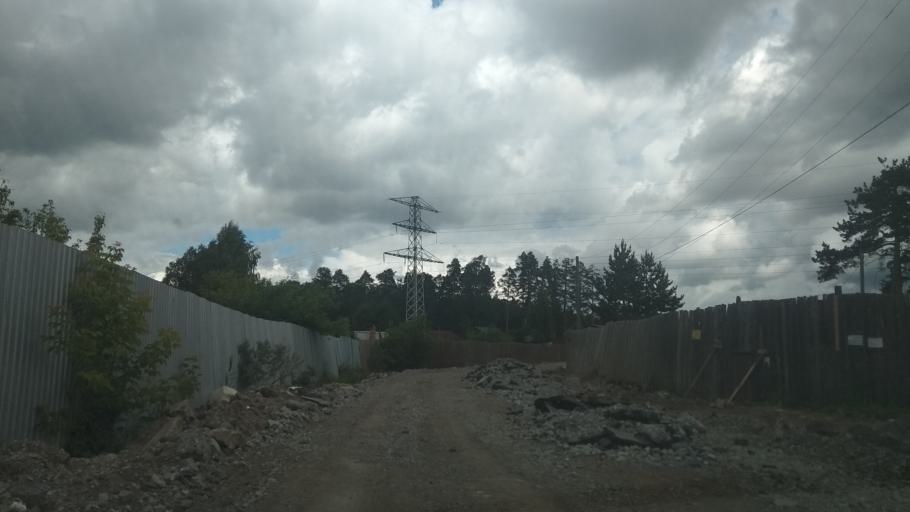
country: RU
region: Sverdlovsk
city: Verkhnyaya Pyshma
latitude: 56.9203
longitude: 60.5716
